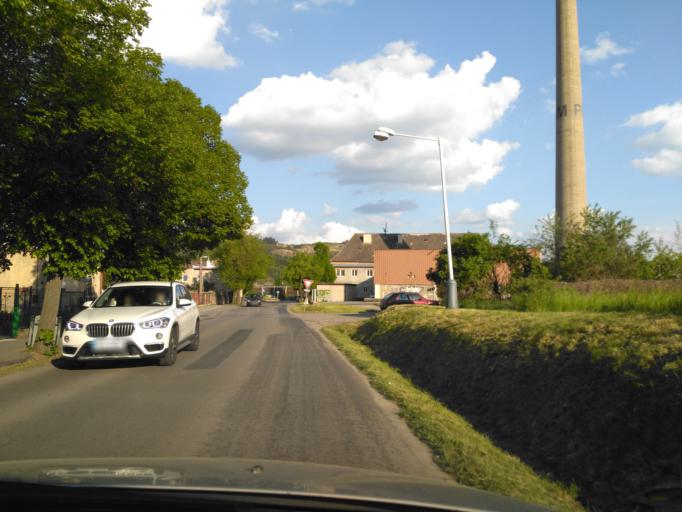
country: CZ
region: Central Bohemia
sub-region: Okres Beroun
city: Kraluv Dvur
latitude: 49.9471
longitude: 14.0334
